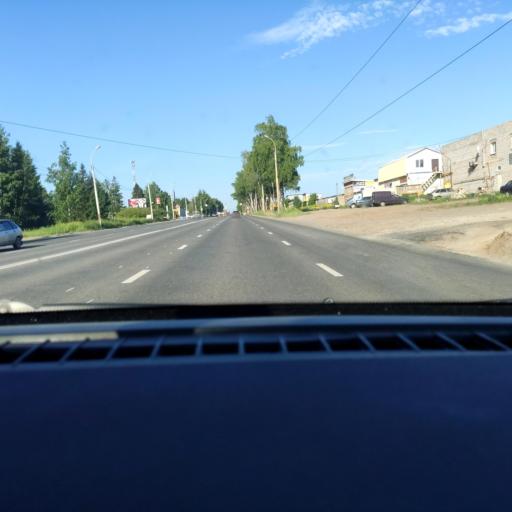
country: RU
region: Udmurtiya
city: Khokhryaki
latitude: 56.9036
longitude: 53.3307
